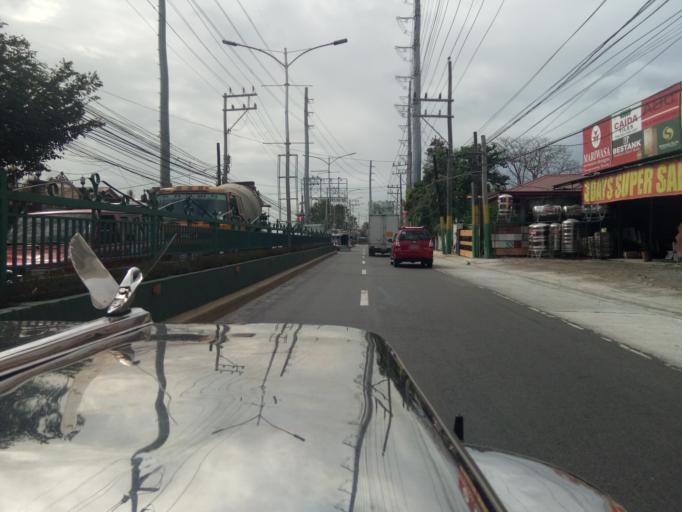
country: PH
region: Calabarzon
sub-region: Province of Cavite
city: Dasmarinas
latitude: 14.3163
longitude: 120.9443
